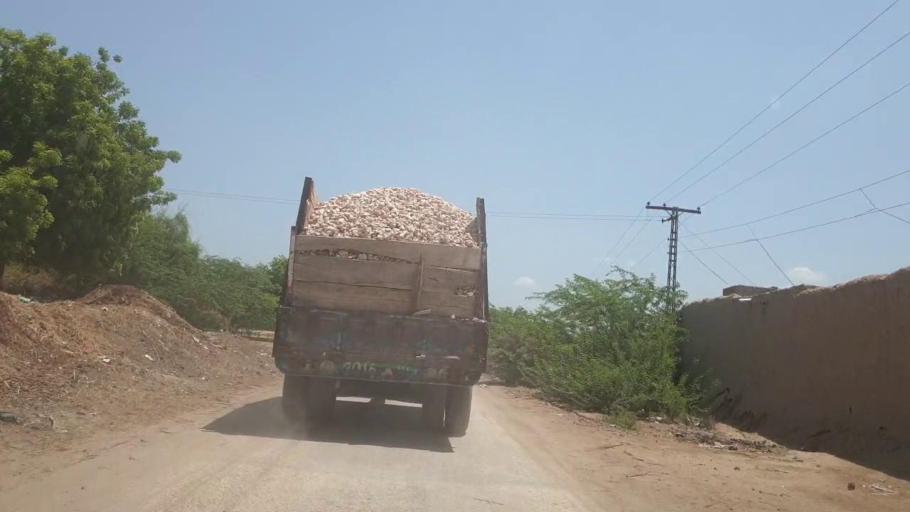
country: PK
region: Sindh
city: Pano Aqil
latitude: 27.6625
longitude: 69.1694
